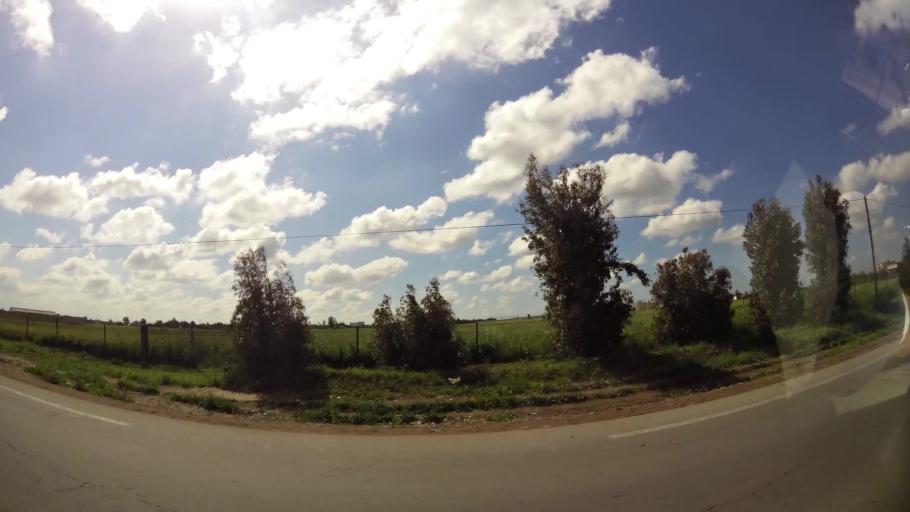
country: MA
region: Grand Casablanca
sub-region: Mediouna
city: Mediouna
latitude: 33.4287
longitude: -7.5229
